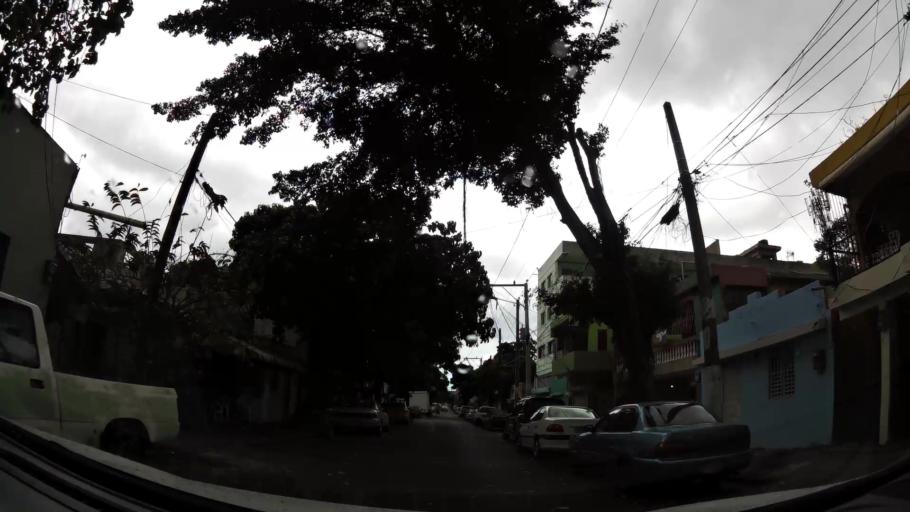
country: DO
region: Nacional
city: San Carlos
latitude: 18.4903
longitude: -69.9111
